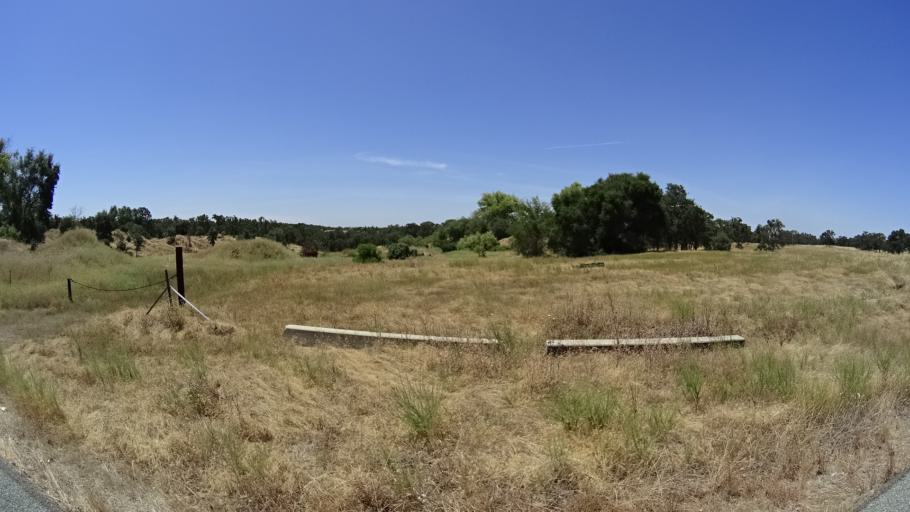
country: US
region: California
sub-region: Calaveras County
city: Rancho Calaveras
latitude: 38.2060
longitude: -120.9485
